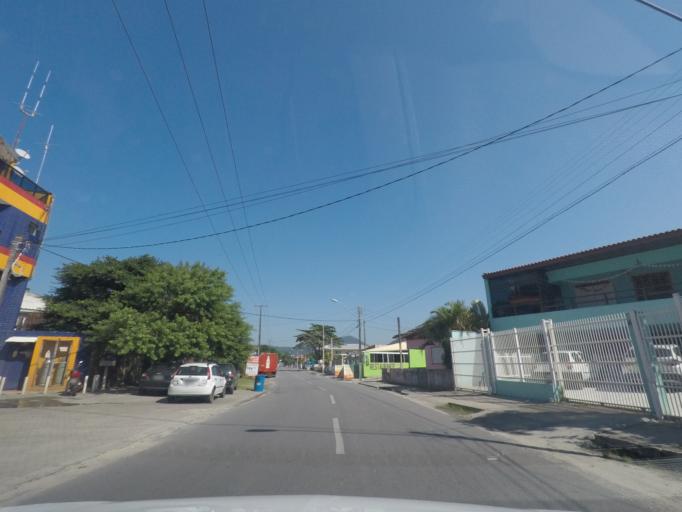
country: BR
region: Parana
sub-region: Guaratuba
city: Guaratuba
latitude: -25.8129
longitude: -48.5340
